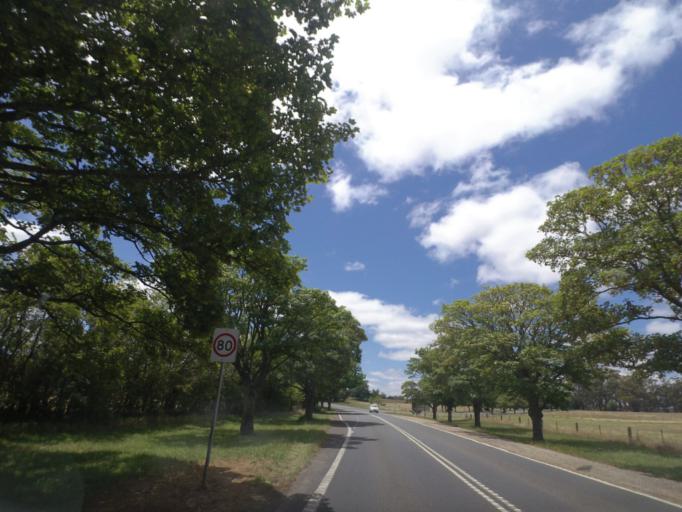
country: AU
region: Victoria
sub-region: Mount Alexander
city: Castlemaine
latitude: -37.3358
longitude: 144.1642
